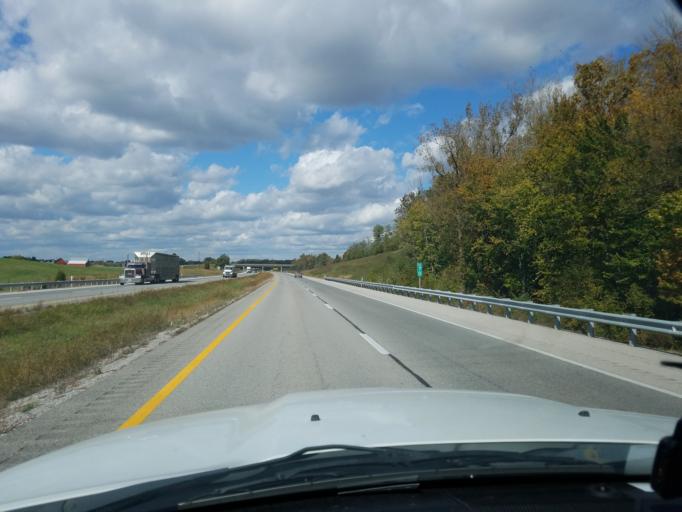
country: US
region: Kentucky
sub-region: Daviess County
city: Masonville
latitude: 37.7138
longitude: -87.0485
